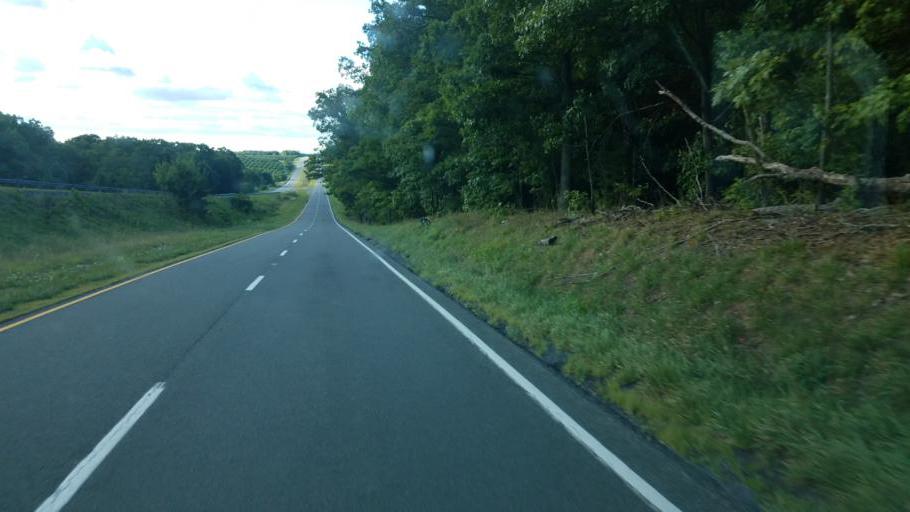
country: US
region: Virginia
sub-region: Frederick County
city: Shawnee Land
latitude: 39.3972
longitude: -78.3082
